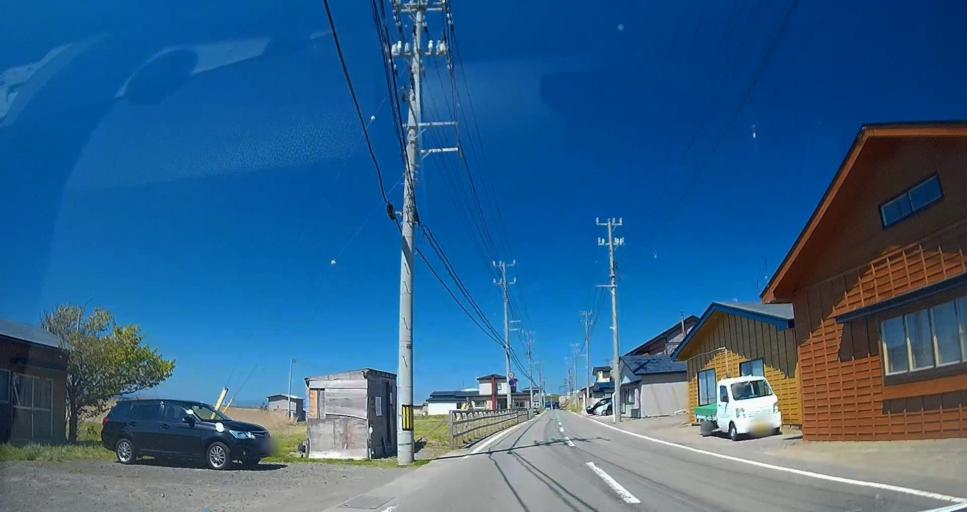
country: JP
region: Hokkaido
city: Hakodate
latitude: 41.4989
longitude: 140.9079
